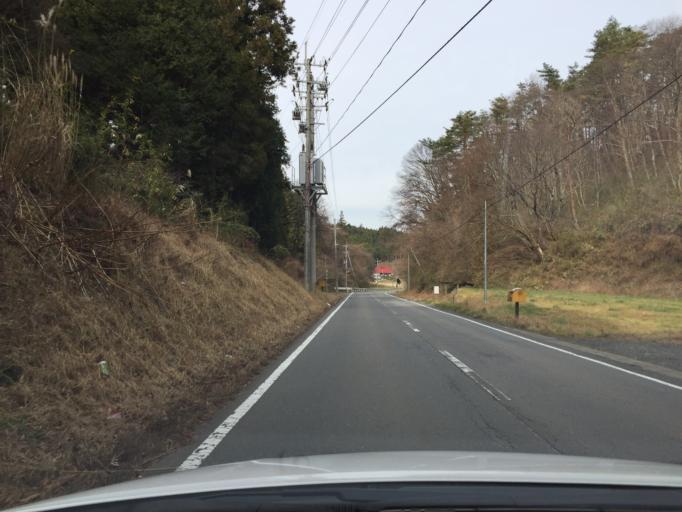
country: JP
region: Fukushima
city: Ishikawa
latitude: 37.2009
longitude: 140.6278
